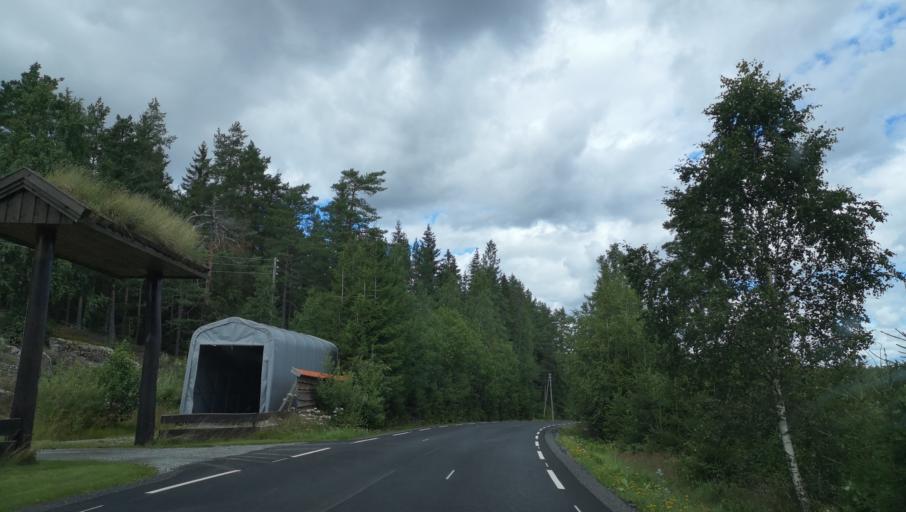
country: NO
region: Ostfold
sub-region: Hobol
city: Elvestad
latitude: 59.6852
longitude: 10.9351
